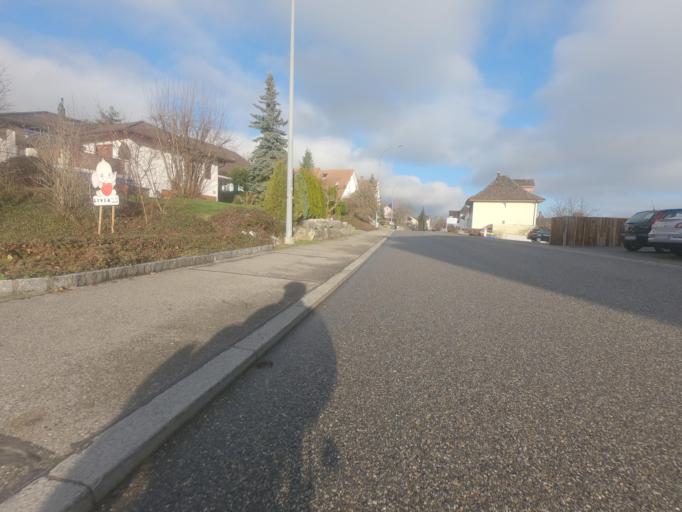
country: CH
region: Solothurn
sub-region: Bezirk Lebern
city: Bettlach
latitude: 47.1999
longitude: 7.4185
